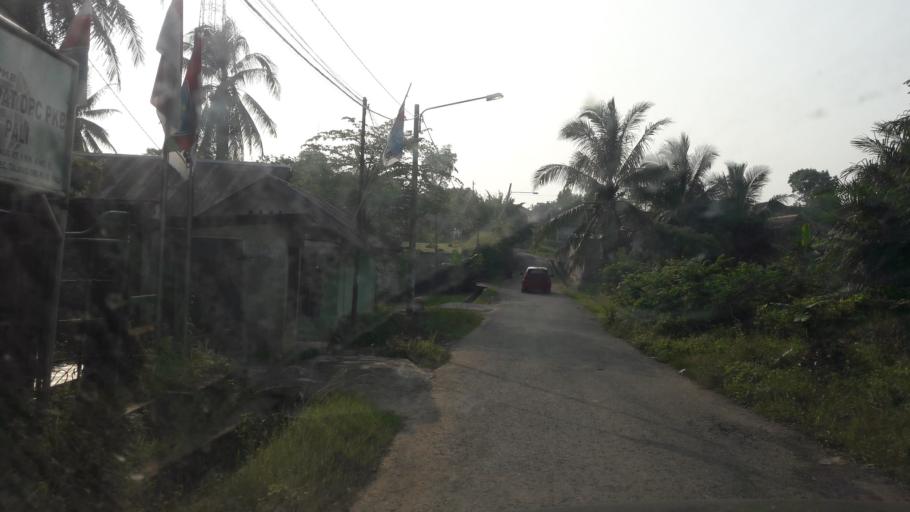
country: ID
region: South Sumatra
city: Gunungmegang Dalam
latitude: -3.2703
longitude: 103.8331
